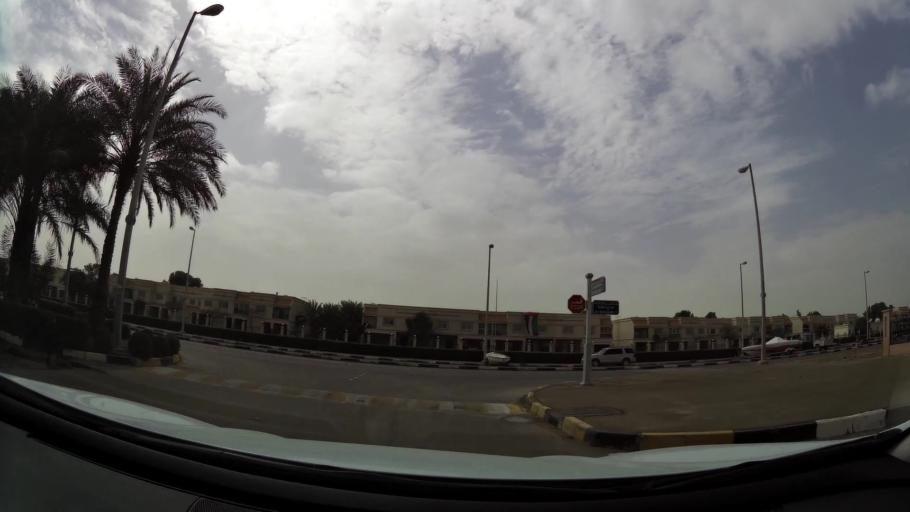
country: AE
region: Abu Dhabi
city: Abu Dhabi
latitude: 24.3929
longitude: 54.4977
